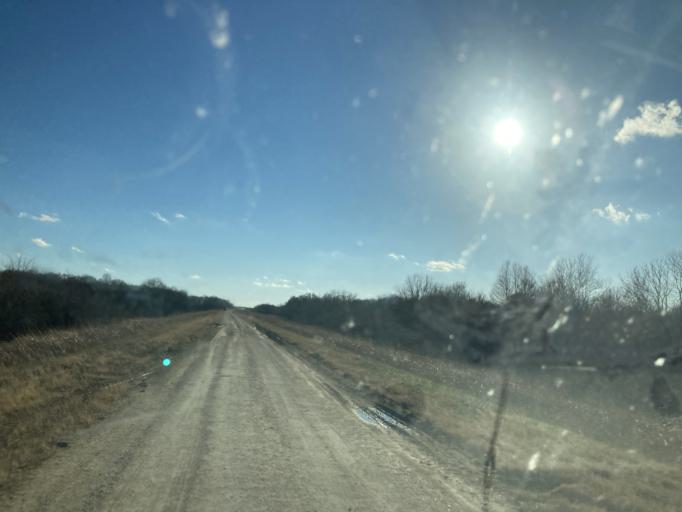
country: US
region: Mississippi
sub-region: Yazoo County
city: Yazoo City
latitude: 32.9260
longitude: -90.5505
